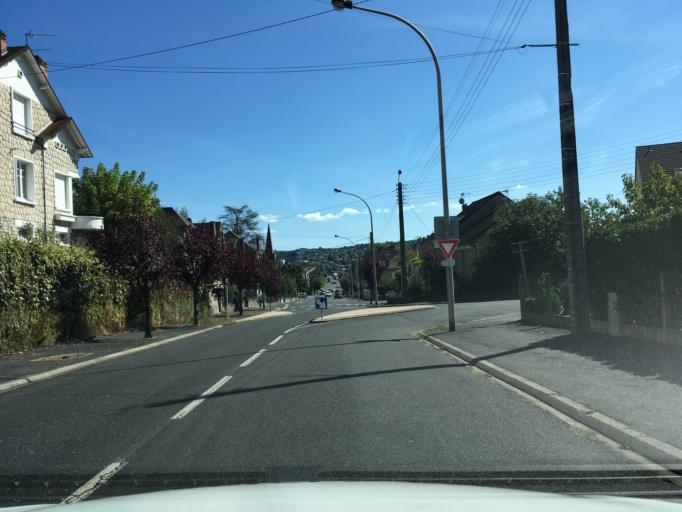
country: FR
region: Limousin
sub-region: Departement de la Correze
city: Brive-la-Gaillarde
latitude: 45.1673
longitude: 1.5187
